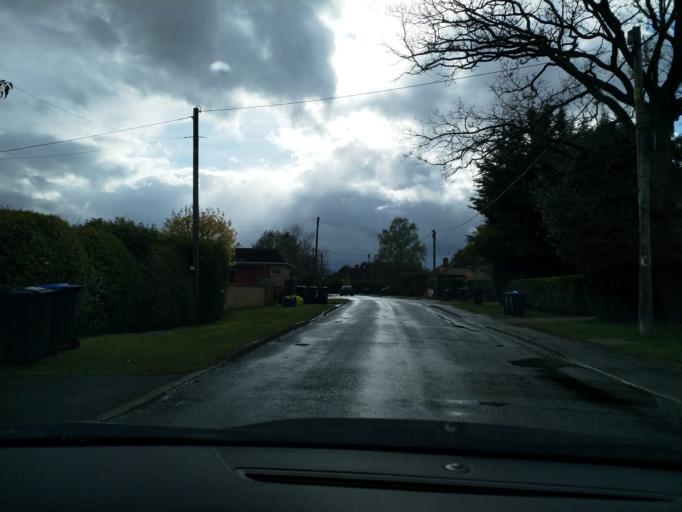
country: GB
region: England
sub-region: Oxfordshire
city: North Leigh
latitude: 51.8137
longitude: -1.4343
